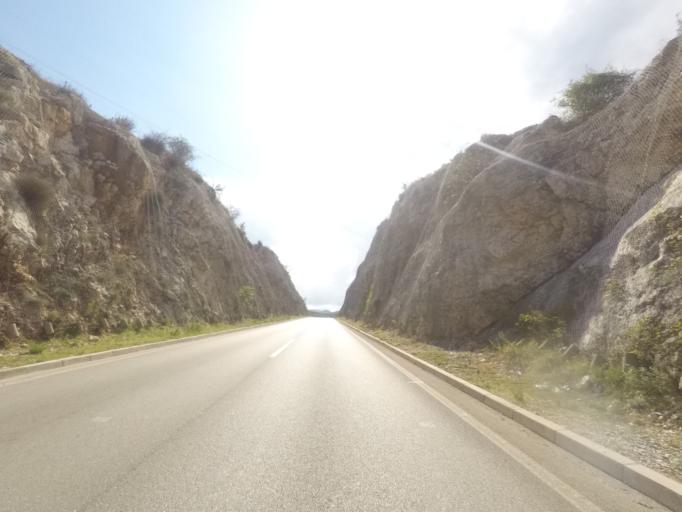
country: BA
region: Republika Srpska
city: Trebinje
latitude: 42.6811
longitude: 18.3386
